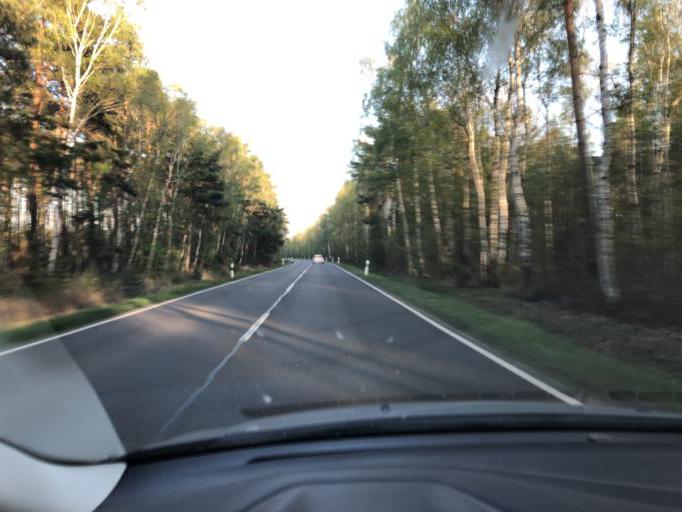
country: DE
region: Brandenburg
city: Welzow
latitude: 51.5481
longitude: 14.1580
